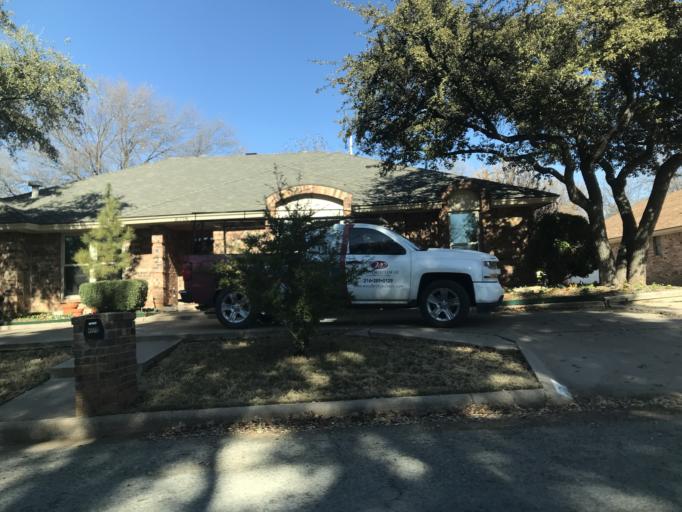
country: US
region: Texas
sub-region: Taylor County
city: Abilene
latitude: 32.3835
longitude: -99.7585
